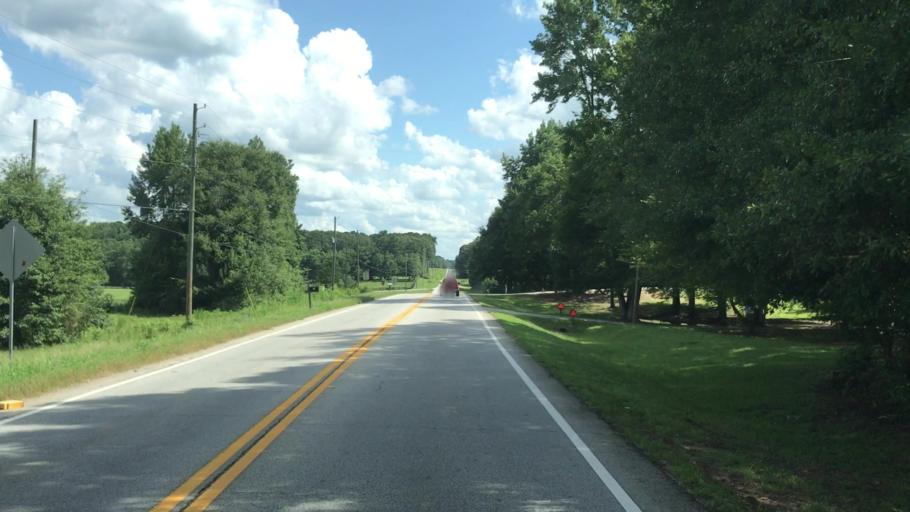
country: US
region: Georgia
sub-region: Walton County
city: Walnut Grove
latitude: 33.7052
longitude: -83.8513
